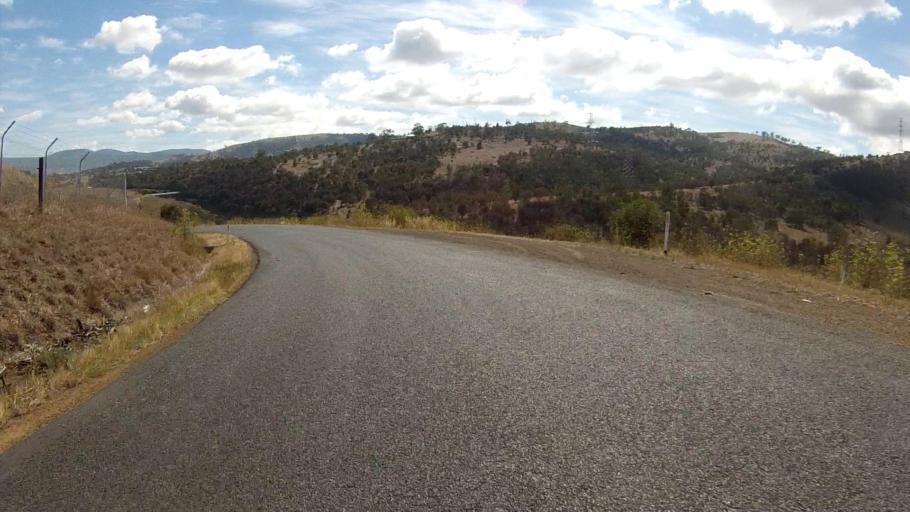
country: AU
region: Tasmania
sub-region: Brighton
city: Bridgewater
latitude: -42.7356
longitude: 147.2592
